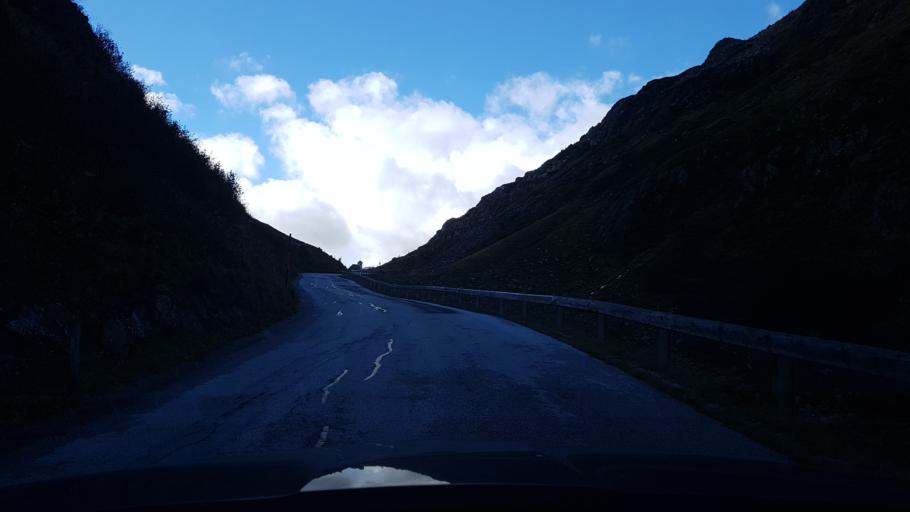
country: AT
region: Styria
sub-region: Politischer Bezirk Liezen
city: Sankt Nikolai im Solktal
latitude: 47.2742
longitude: 14.0811
